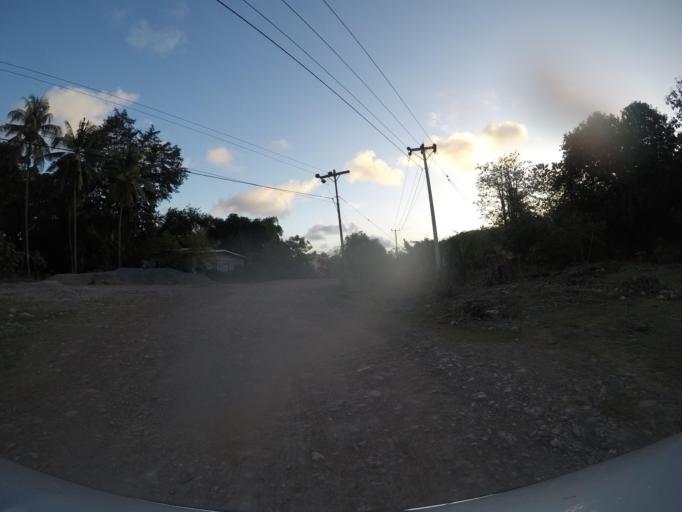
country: TL
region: Baucau
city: Venilale
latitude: -8.7502
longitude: 126.6953
